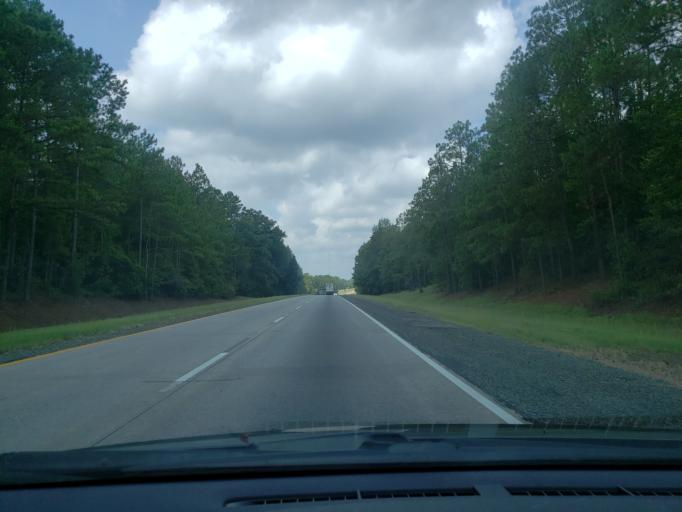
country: US
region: Georgia
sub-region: Treutlen County
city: Soperton
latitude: 32.4350
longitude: -82.6443
